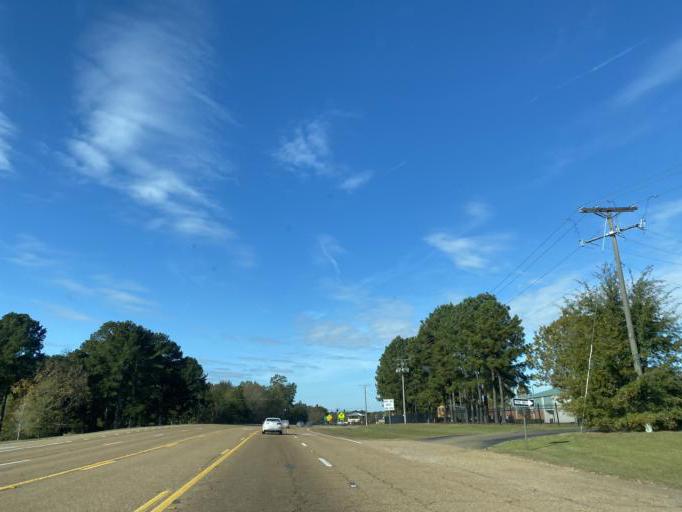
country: US
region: Mississippi
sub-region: Madison County
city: Madison
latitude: 32.4727
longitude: -90.1452
